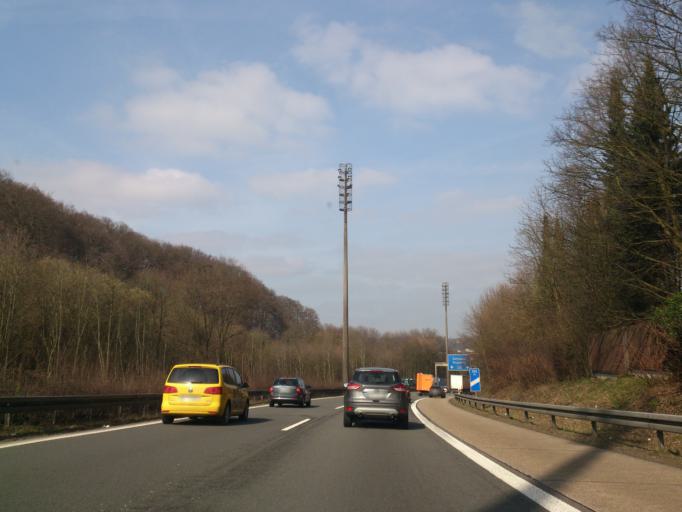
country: DE
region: North Rhine-Westphalia
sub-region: Regierungsbezirk Dusseldorf
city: Solingen
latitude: 51.2299
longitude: 7.0885
